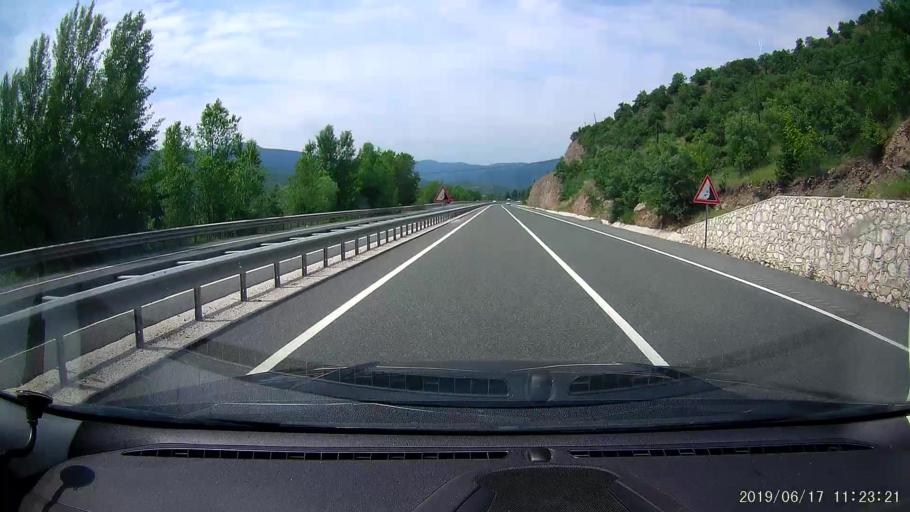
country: TR
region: Cankiri
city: Ilgaz
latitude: 40.8887
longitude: 33.7338
